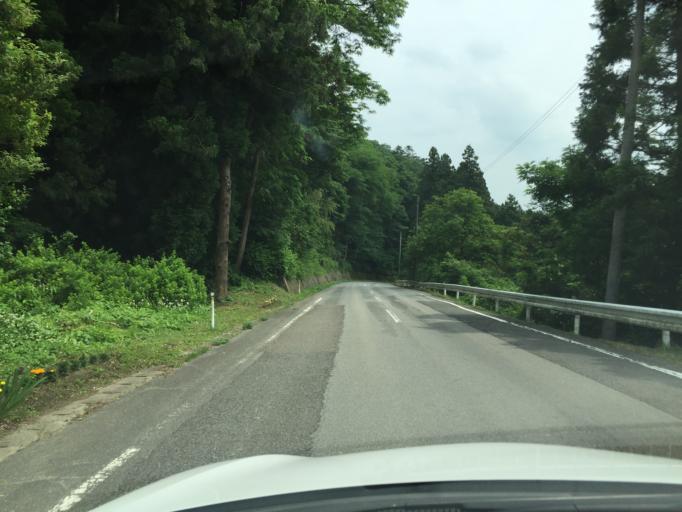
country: JP
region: Fukushima
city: Miharu
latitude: 37.3024
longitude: 140.5408
